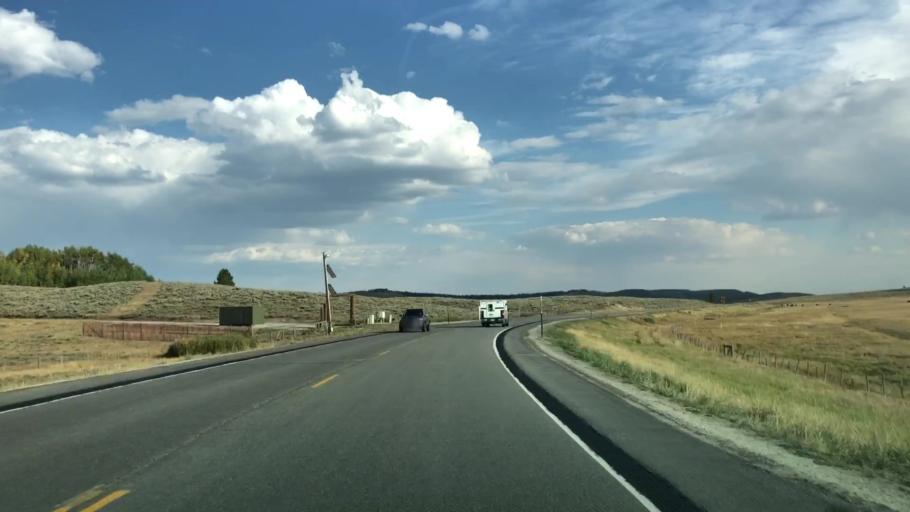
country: US
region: Wyoming
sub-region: Sublette County
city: Pinedale
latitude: 43.1309
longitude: -110.1924
